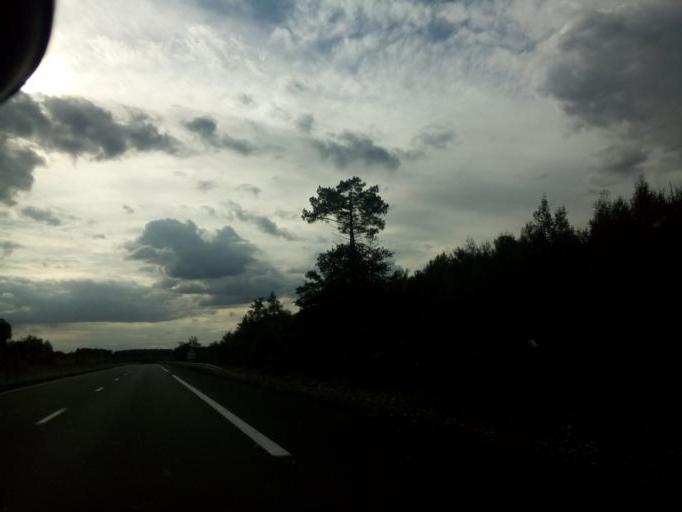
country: FR
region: Centre
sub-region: Departement du Loir-et-Cher
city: Thesee
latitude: 47.2946
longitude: 1.2575
